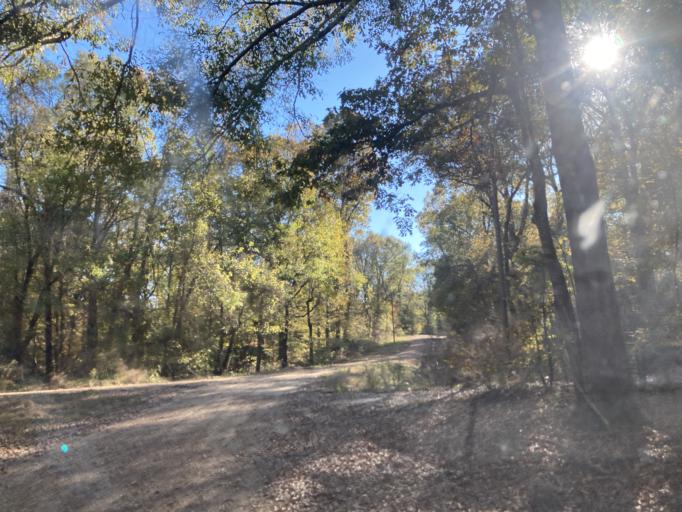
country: US
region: Mississippi
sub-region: Yazoo County
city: Yazoo City
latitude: 32.7442
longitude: -90.4333
